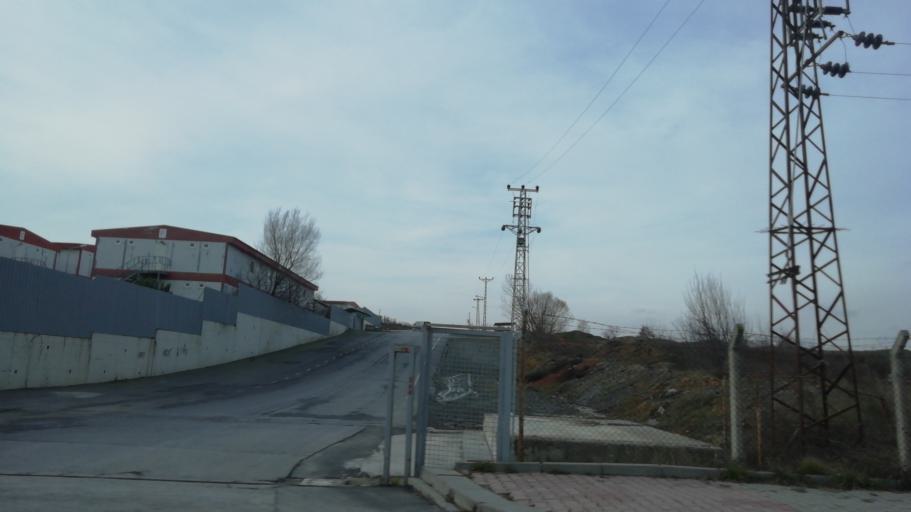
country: TR
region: Istanbul
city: Basaksehir
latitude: 41.1125
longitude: 28.7969
